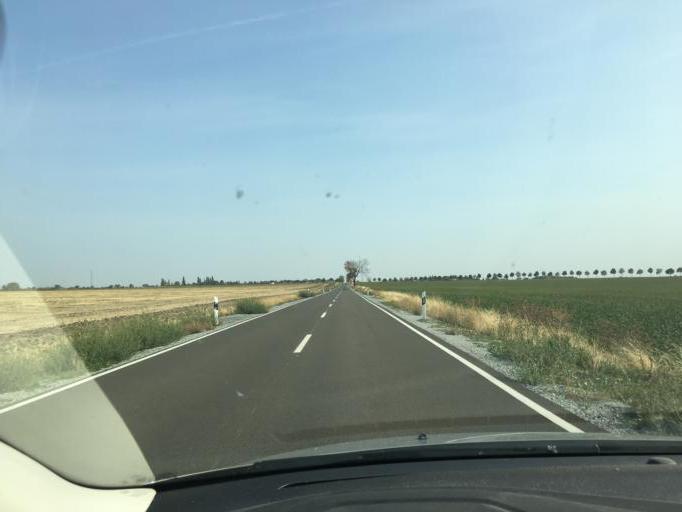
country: DE
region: Saxony-Anhalt
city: Wulfen
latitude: 51.7956
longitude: 11.8651
